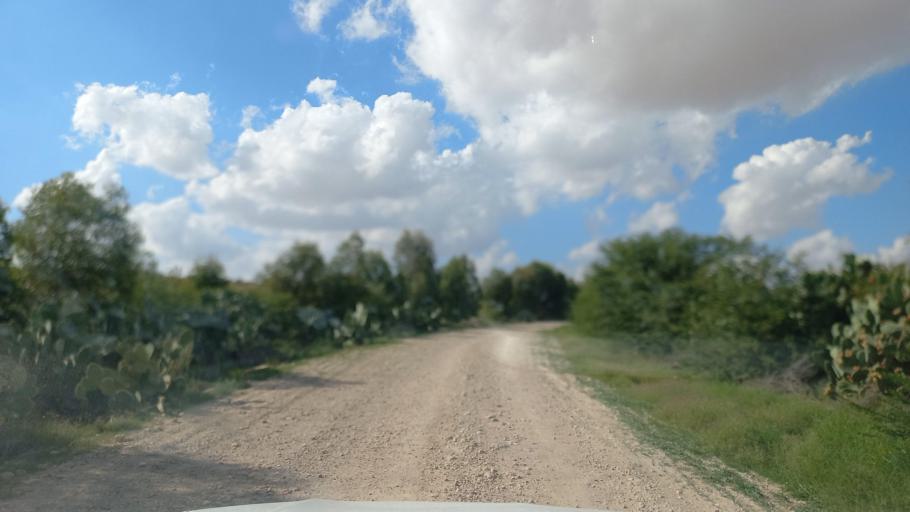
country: TN
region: Al Qasrayn
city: Sbiba
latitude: 35.3373
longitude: 9.0791
